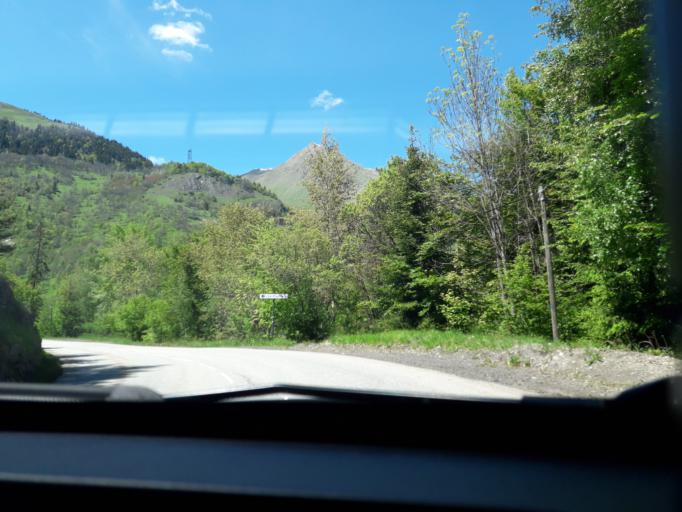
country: FR
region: Rhone-Alpes
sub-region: Departement de la Savoie
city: Saint-Martin-de-Belleville
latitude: 45.4215
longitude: 6.4861
